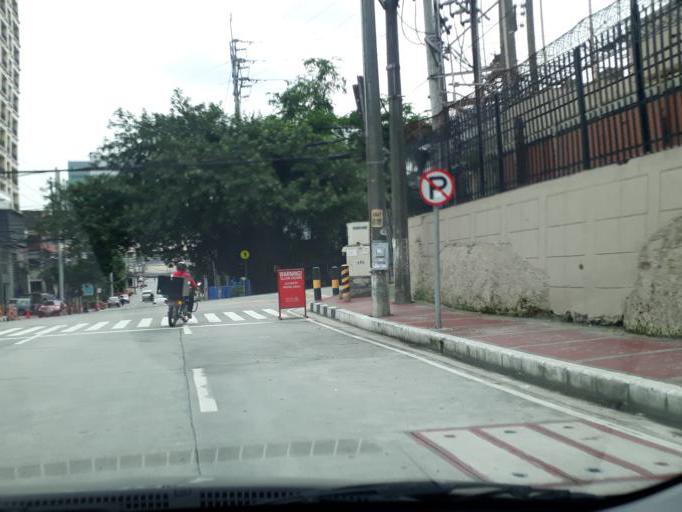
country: PH
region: Metro Manila
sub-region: Quezon City
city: Quezon City
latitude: 14.6407
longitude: 121.0365
